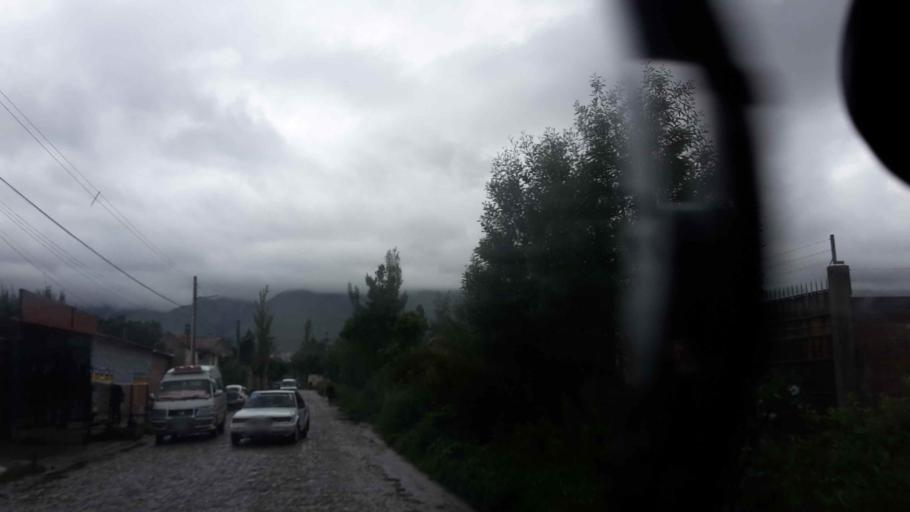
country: BO
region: Cochabamba
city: Cochabamba
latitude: -17.3631
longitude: -66.2129
